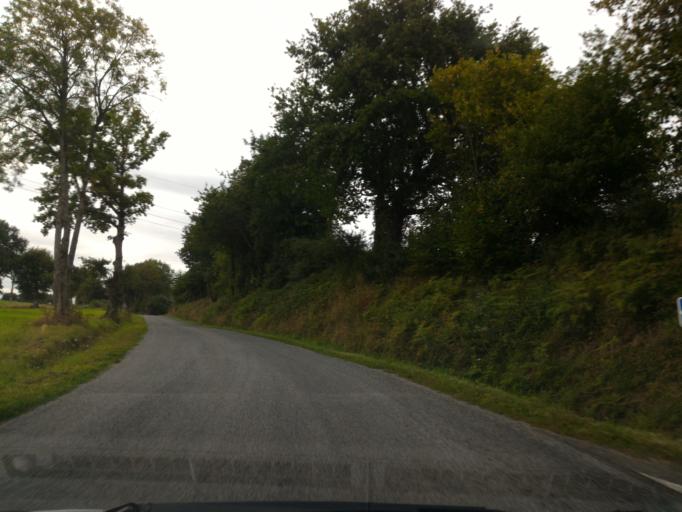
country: FR
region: Poitou-Charentes
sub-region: Departement de la Charente
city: Brigueuil
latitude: 45.9105
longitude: 0.8588
